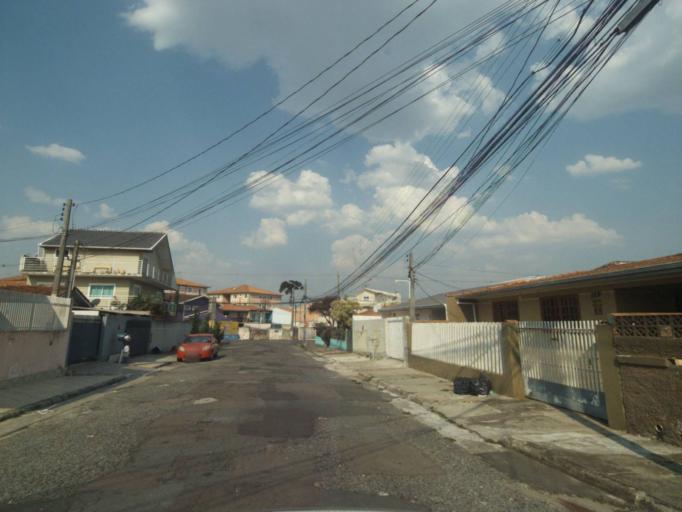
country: BR
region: Parana
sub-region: Sao Jose Dos Pinhais
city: Sao Jose dos Pinhais
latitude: -25.5367
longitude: -49.2365
